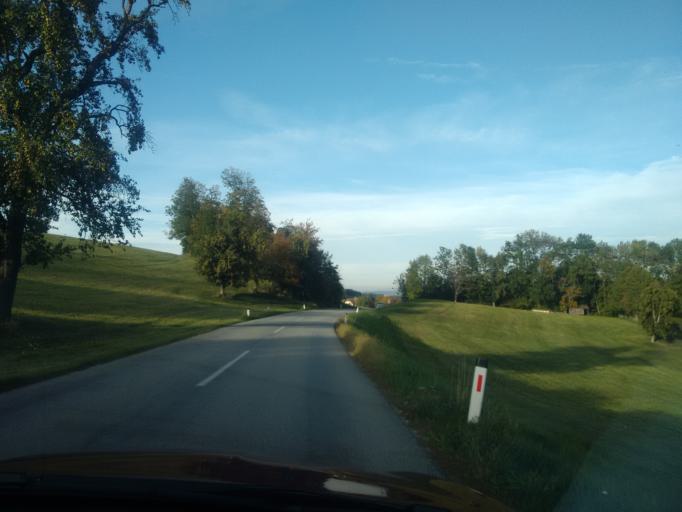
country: AT
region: Upper Austria
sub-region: Politischer Bezirk Vocklabruck
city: Wolfsegg am Hausruck
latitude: 48.1125
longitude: 13.6817
